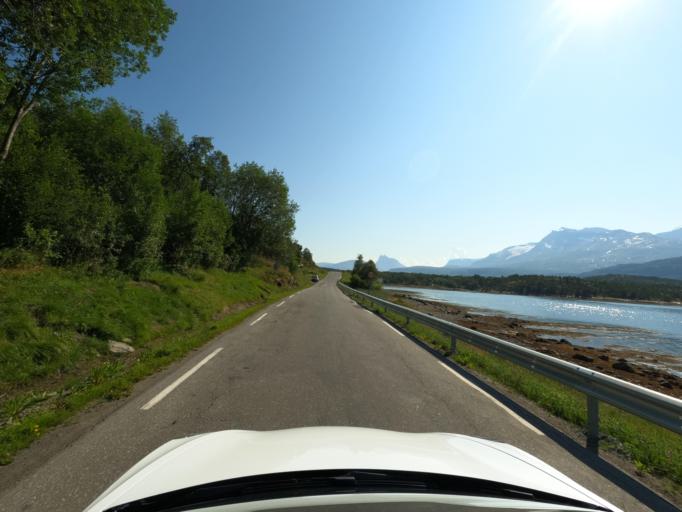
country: NO
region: Nordland
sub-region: Narvik
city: Narvik
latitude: 68.3309
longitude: 17.2809
